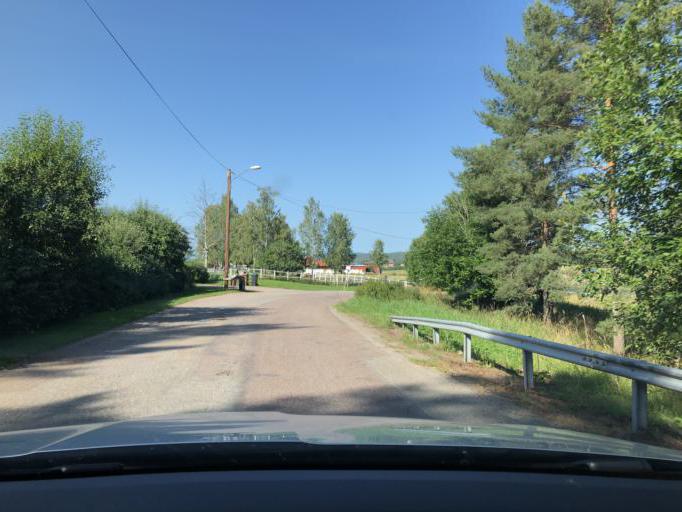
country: SE
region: Dalarna
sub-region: Hedemora Kommun
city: Hedemora
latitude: 60.3648
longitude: 15.9251
